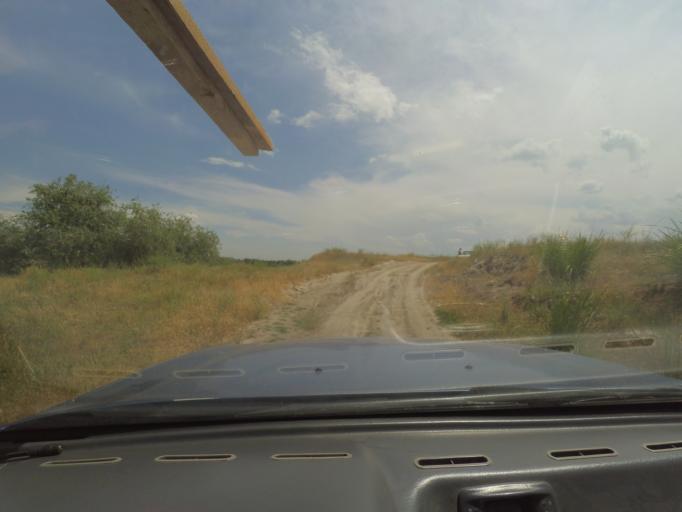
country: TJ
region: Viloyati Sughd
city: Buston
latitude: 40.5404
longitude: 69.0790
